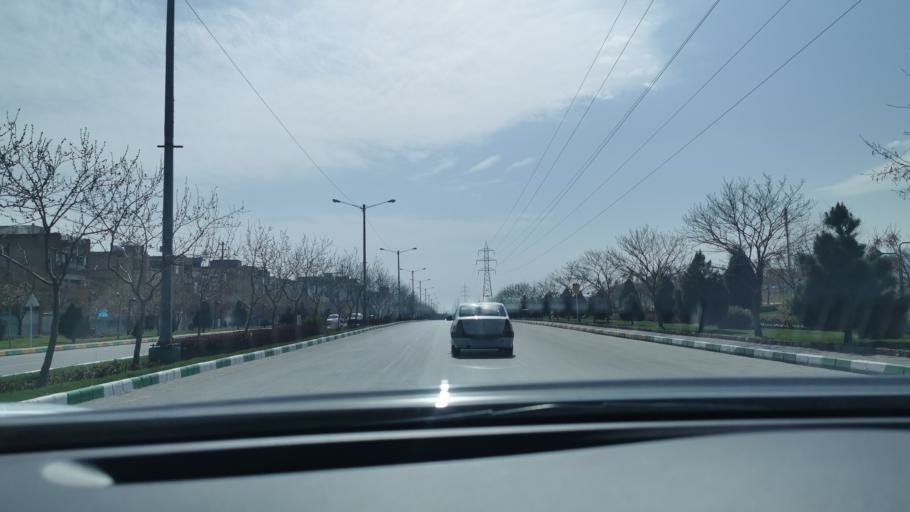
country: IR
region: Razavi Khorasan
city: Mashhad
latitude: 36.2877
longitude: 59.5354
